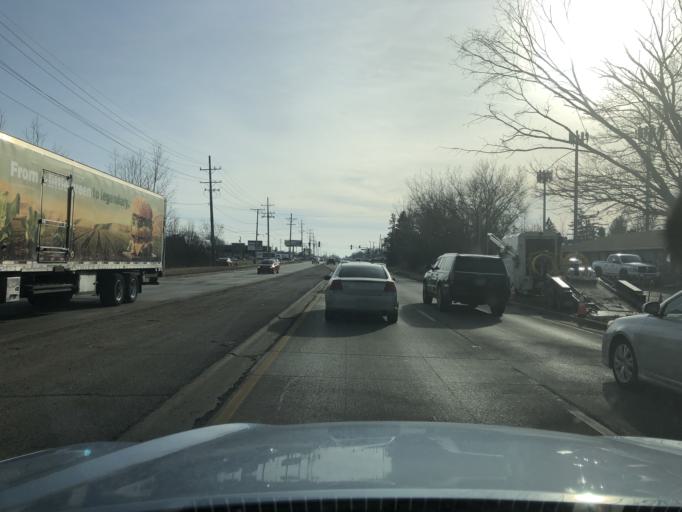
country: US
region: Illinois
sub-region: DuPage County
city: Roselle
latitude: 42.0001
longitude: -88.0802
